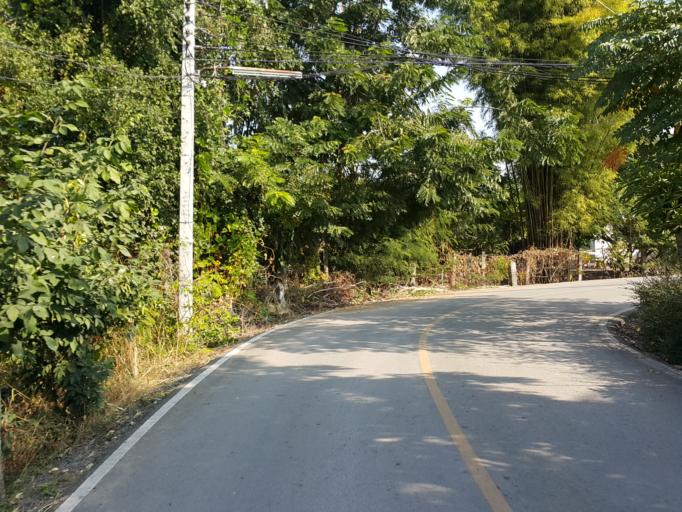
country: TH
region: Chiang Mai
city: San Kamphaeng
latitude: 18.6952
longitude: 99.1119
